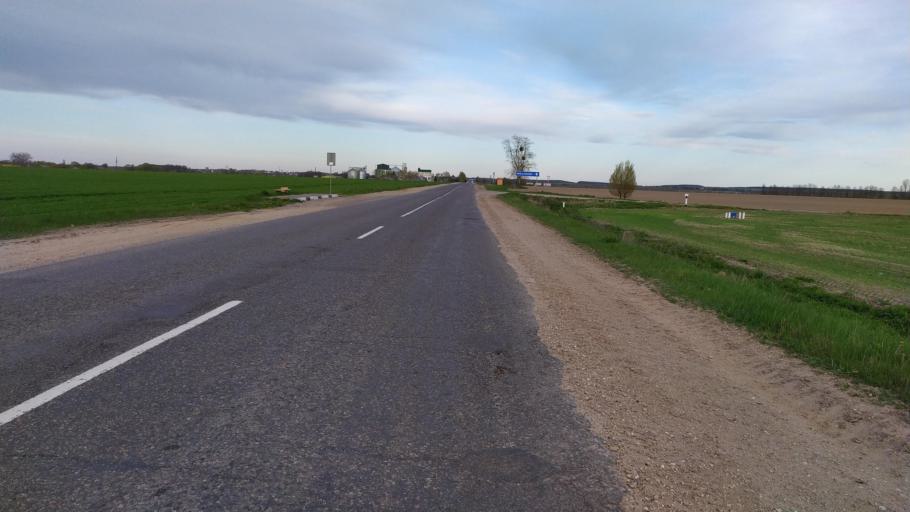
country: BY
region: Brest
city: Kamyanyets
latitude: 52.4031
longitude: 23.7648
